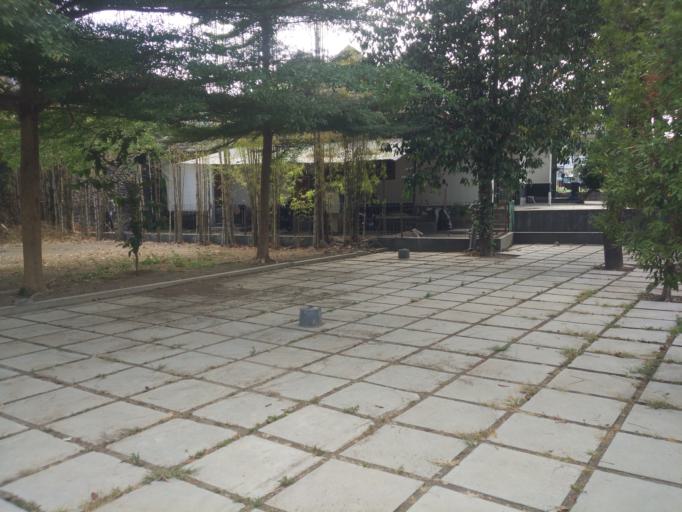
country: ID
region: Daerah Istimewa Yogyakarta
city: Sleman
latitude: -7.6873
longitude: 110.4183
